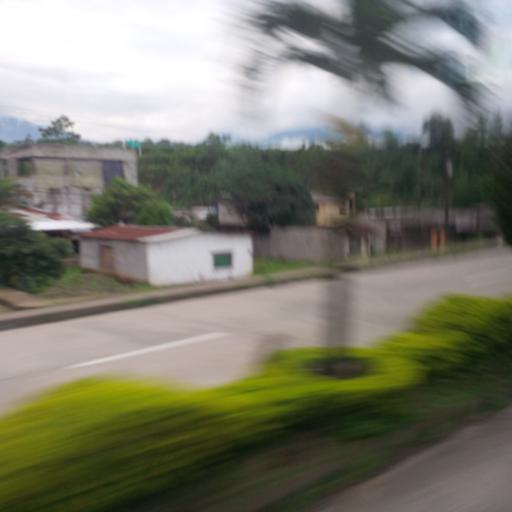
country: EC
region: Chimborazo
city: Alausi
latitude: -2.2095
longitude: -79.1352
